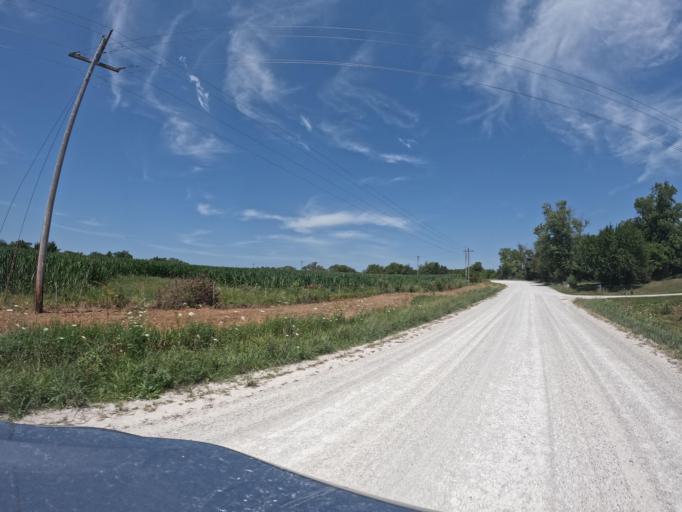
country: US
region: Iowa
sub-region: Henry County
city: Mount Pleasant
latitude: 40.9036
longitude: -91.5363
